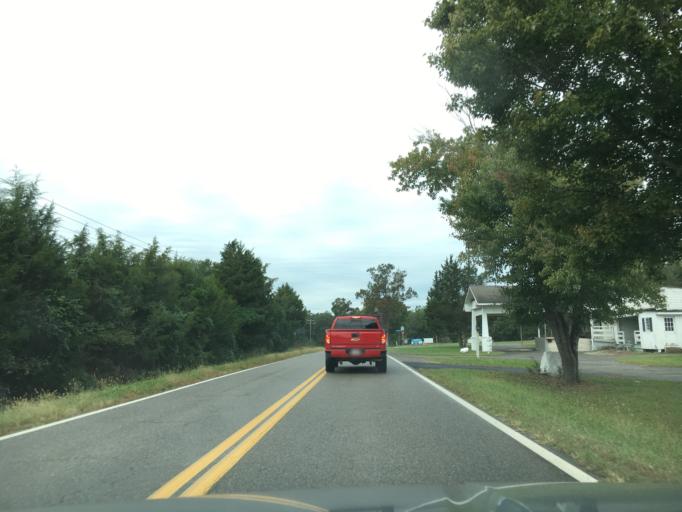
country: US
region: Virginia
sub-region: Goochland County
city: Goochland
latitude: 37.7598
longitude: -77.8734
